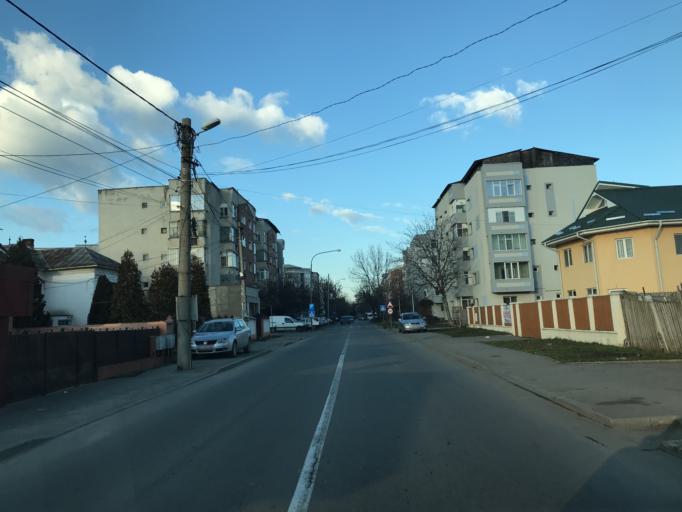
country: RO
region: Olt
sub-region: Municipiul Slatina
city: Slatina
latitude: 44.4161
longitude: 24.3802
